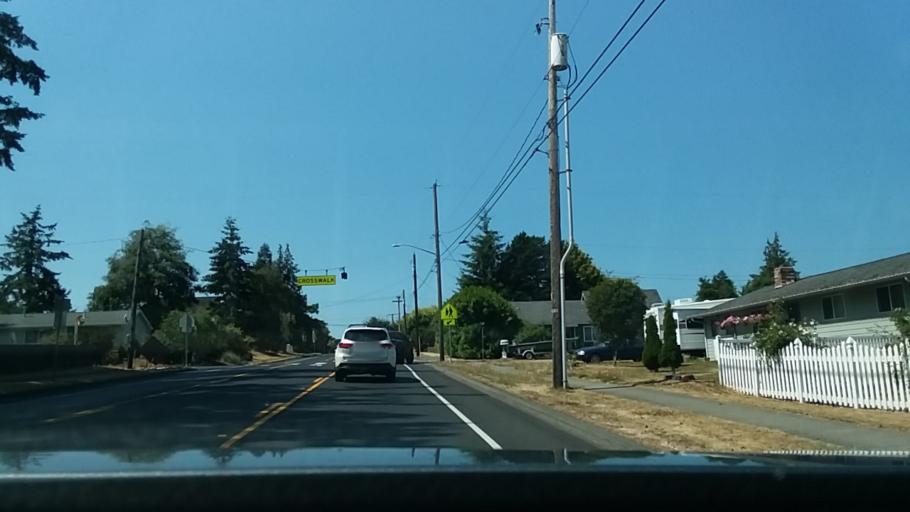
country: US
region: Washington
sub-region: Skagit County
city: Anacortes
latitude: 48.5127
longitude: -122.6181
